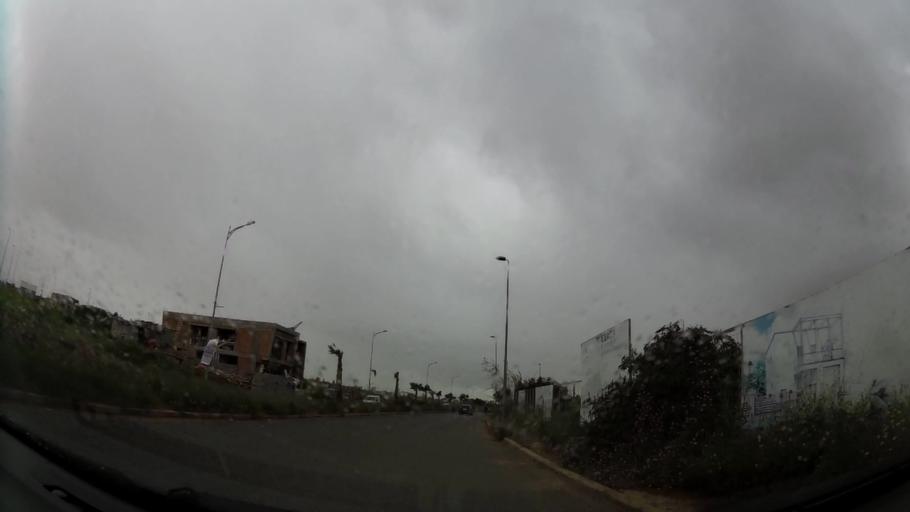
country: MA
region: Grand Casablanca
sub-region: Casablanca
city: Casablanca
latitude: 33.5242
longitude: -7.6224
